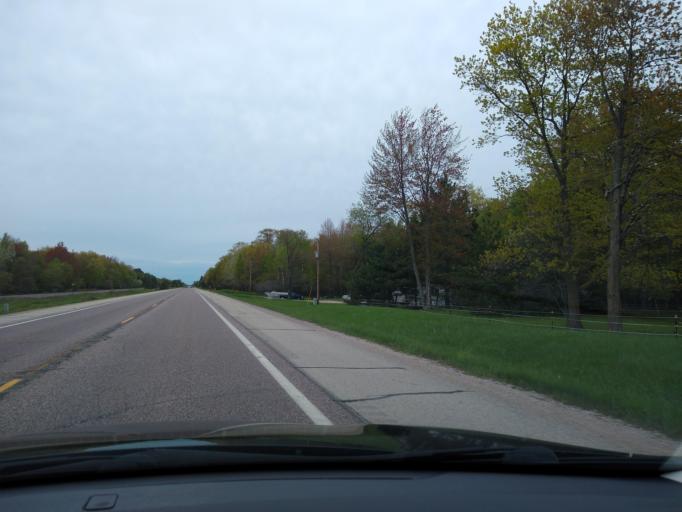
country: US
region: Michigan
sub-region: Delta County
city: Gladstone
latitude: 45.8716
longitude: -87.0637
